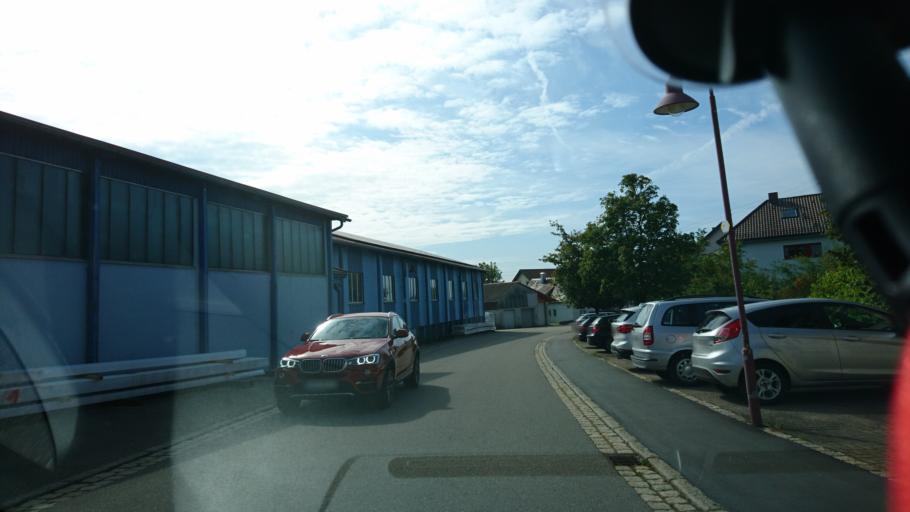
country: DE
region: Baden-Wuerttemberg
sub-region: Regierungsbezirk Stuttgart
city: Mainhardt
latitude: 49.0978
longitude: 9.5770
